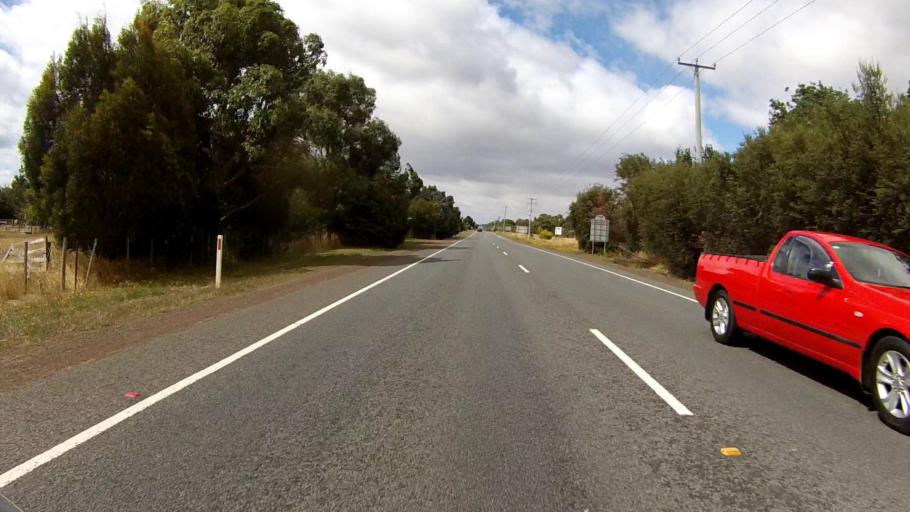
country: AU
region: Tasmania
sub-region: Northern Midlands
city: Evandale
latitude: -41.9428
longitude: 147.4921
